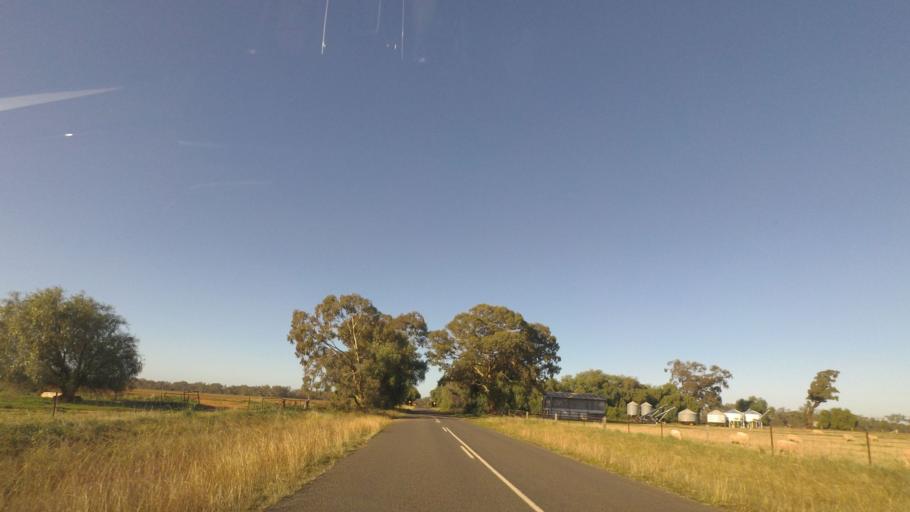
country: AU
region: Victoria
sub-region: Greater Bendigo
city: Epsom
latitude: -36.6465
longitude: 144.5347
